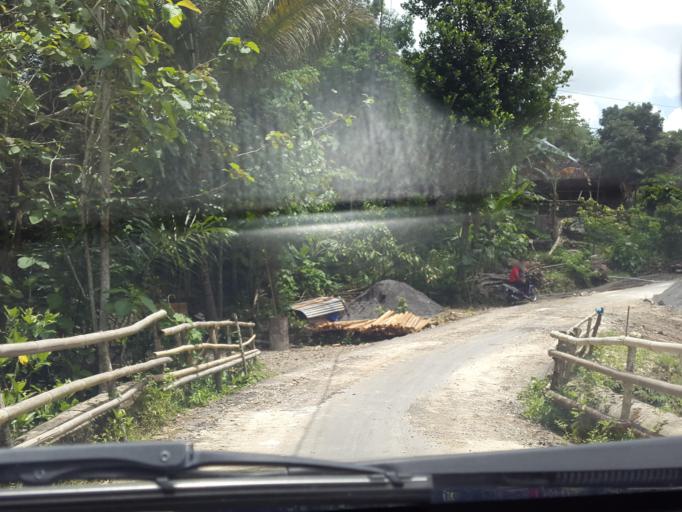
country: ID
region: Daerah Istimewa Yogyakarta
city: Wonosari
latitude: -7.9238
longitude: 110.7403
